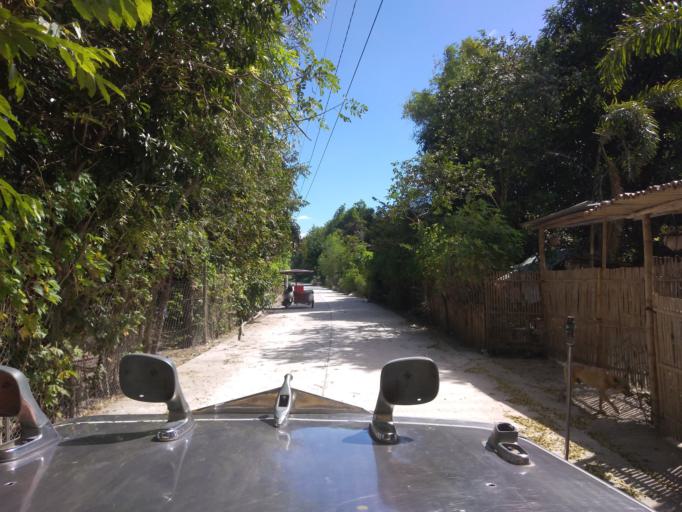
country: PH
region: Central Luzon
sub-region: Province of Pampanga
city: Bacolor
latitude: 15.0140
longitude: 120.6553
